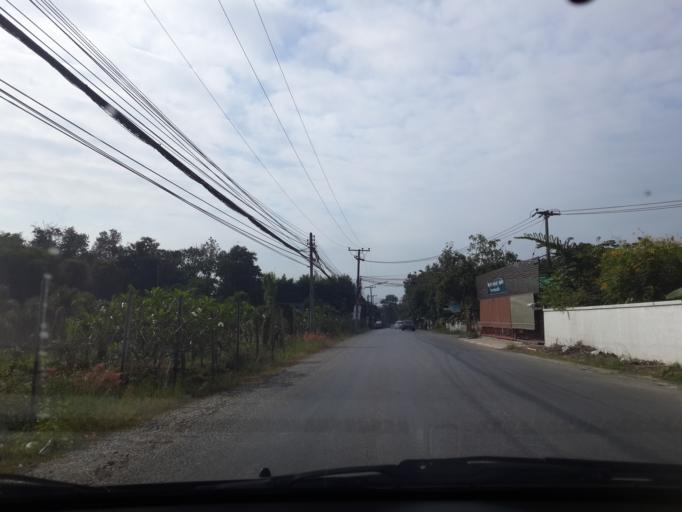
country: TH
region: Chiang Mai
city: San Sai
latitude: 18.9070
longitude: 99.0167
